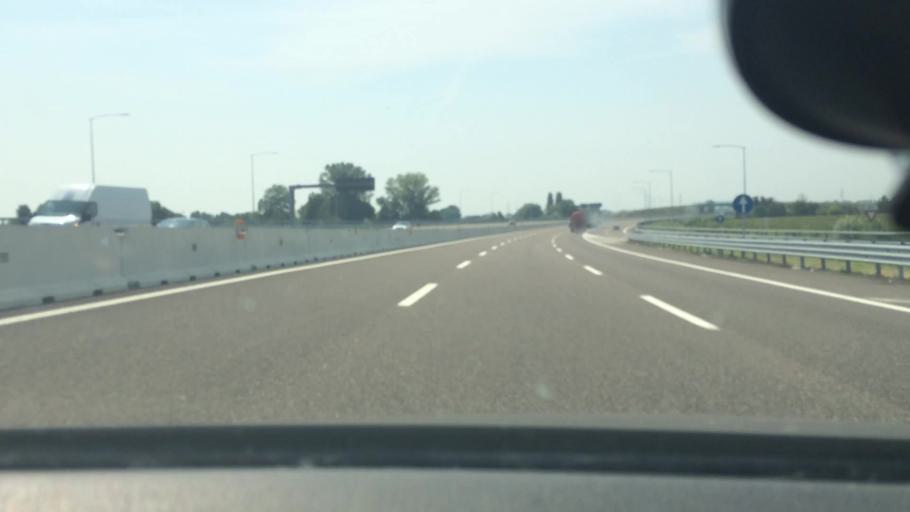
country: IT
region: Lombardy
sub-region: Citta metropolitana di Milano
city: Pozzuolo Martesana
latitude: 45.4997
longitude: 9.4447
